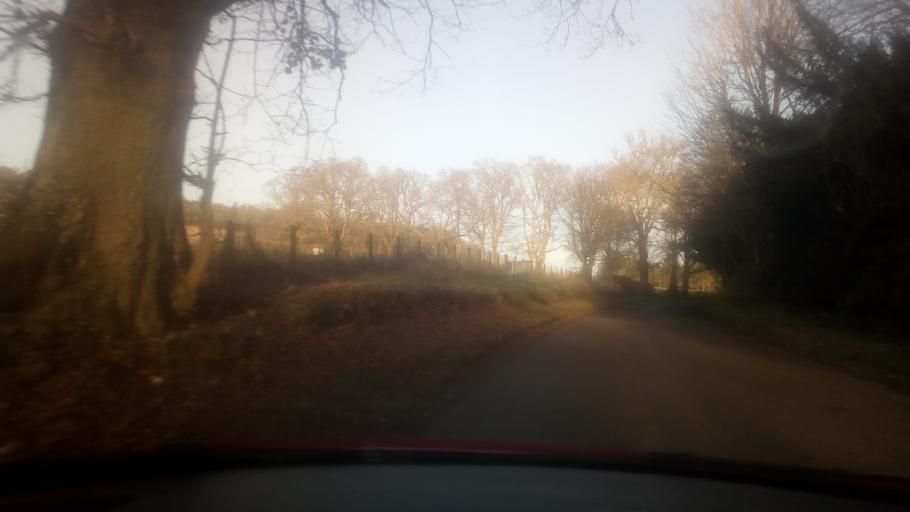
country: GB
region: Scotland
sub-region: The Scottish Borders
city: Jedburgh
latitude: 55.5180
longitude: -2.5603
